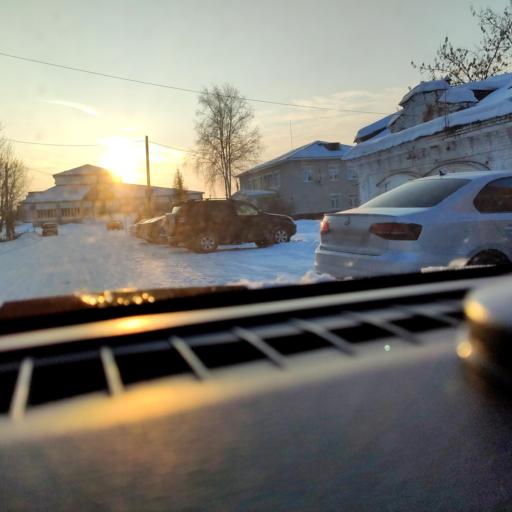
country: RU
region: Perm
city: Orda
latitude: 57.1967
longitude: 56.9029
